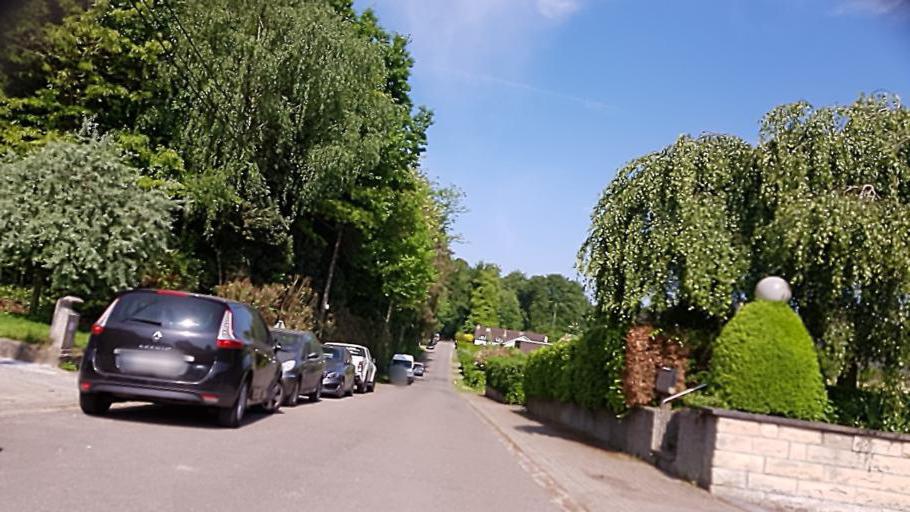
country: BE
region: Flanders
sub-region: Provincie Vlaams-Brabant
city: Tervuren
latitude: 50.8069
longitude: 4.5357
